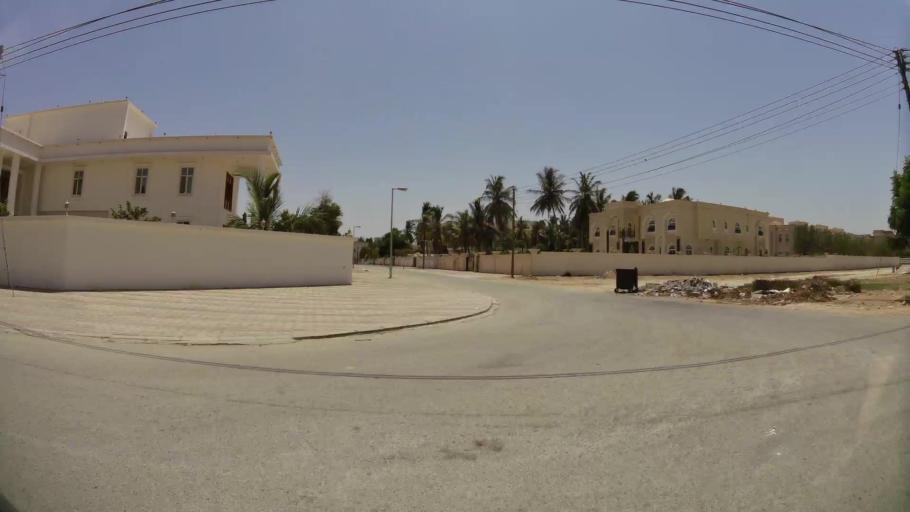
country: OM
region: Zufar
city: Salalah
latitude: 17.0566
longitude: 54.1532
